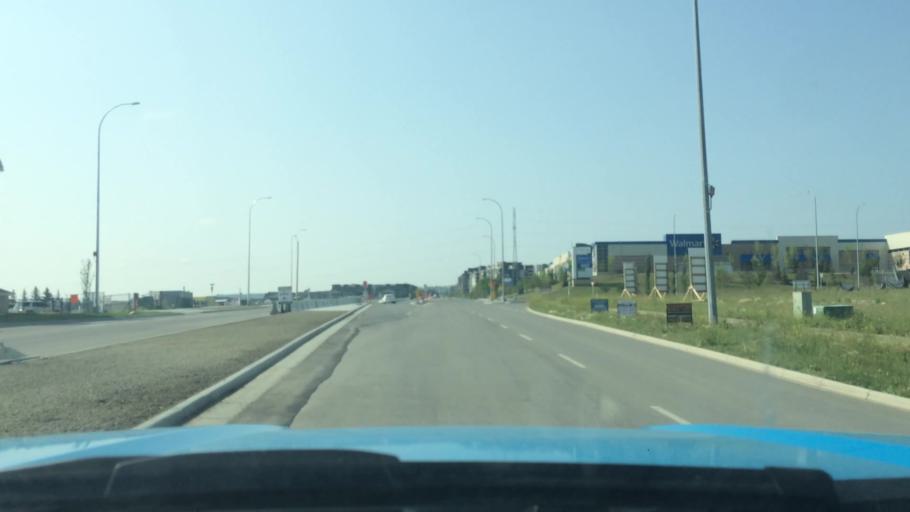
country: CA
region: Alberta
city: Calgary
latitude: 51.1721
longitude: -114.1413
